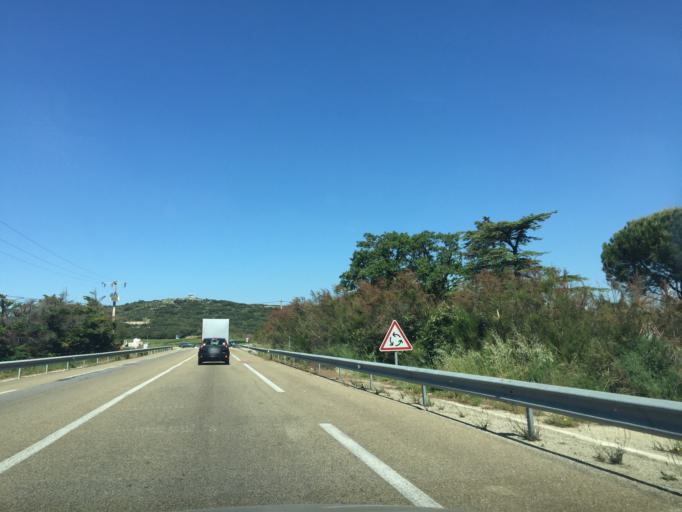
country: FR
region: Languedoc-Roussillon
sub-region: Departement du Gard
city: Saze
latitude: 43.9553
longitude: 4.6570
